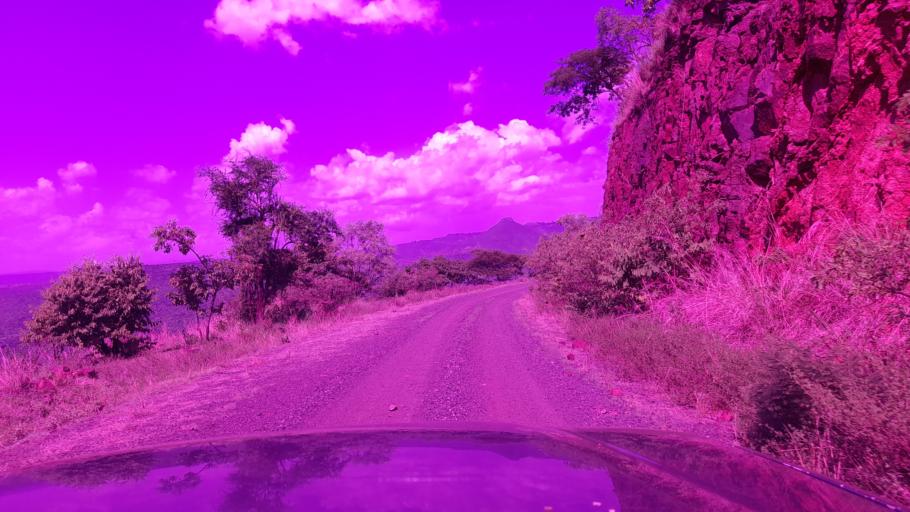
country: ET
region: Southern Nations, Nationalities, and People's Region
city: K'olito
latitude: 7.7804
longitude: 37.5581
